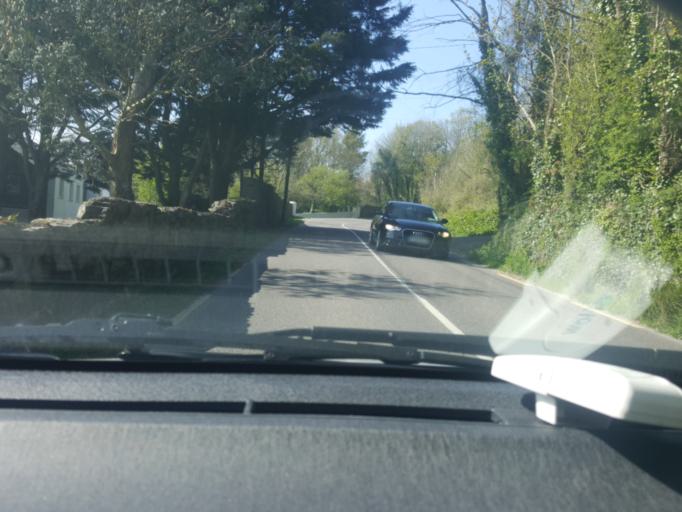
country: IE
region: Munster
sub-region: County Cork
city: Bandon
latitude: 51.7597
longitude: -8.6466
